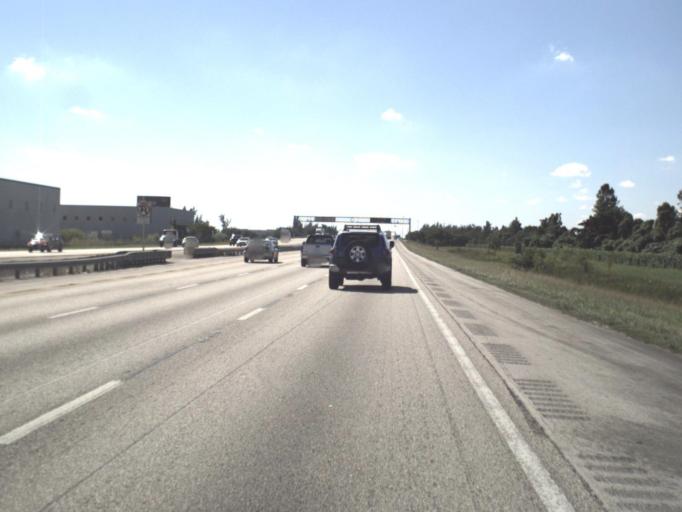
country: US
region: Florida
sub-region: Miami-Dade County
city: Hialeah Gardens
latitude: 25.8883
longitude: -80.3889
